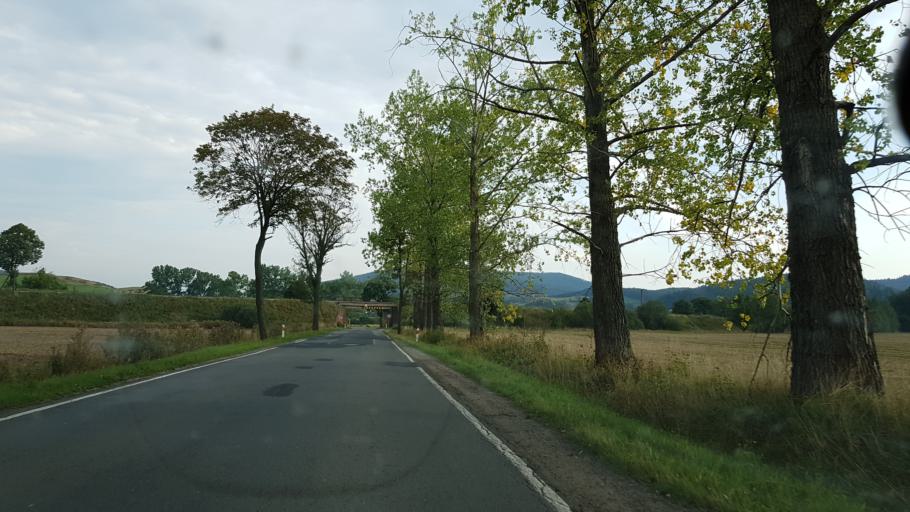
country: PL
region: Lower Silesian Voivodeship
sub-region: Powiat kamiennogorski
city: Marciszow
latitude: 50.8616
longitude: 16.0014
